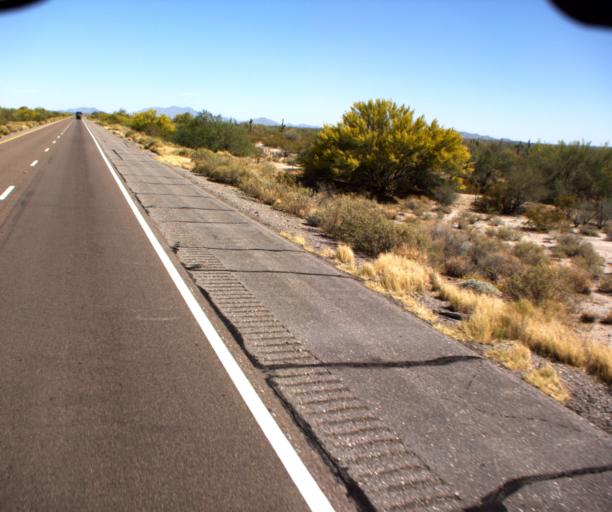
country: US
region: Arizona
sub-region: Maricopa County
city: Gila Bend
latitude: 32.8569
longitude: -112.3823
